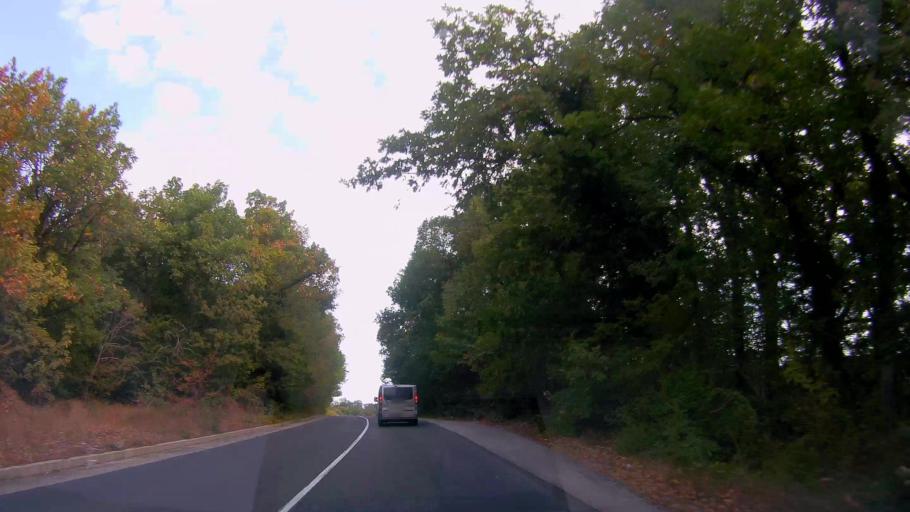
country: BG
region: Burgas
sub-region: Obshtina Primorsko
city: Primorsko
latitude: 42.3215
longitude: 27.7303
